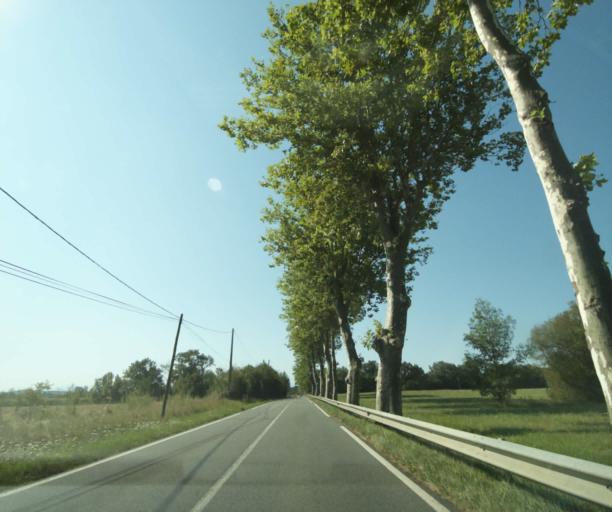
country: FR
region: Midi-Pyrenees
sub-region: Departement de la Haute-Garonne
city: Saint-Sulpice-sur-Leze
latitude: 43.3226
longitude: 1.3226
